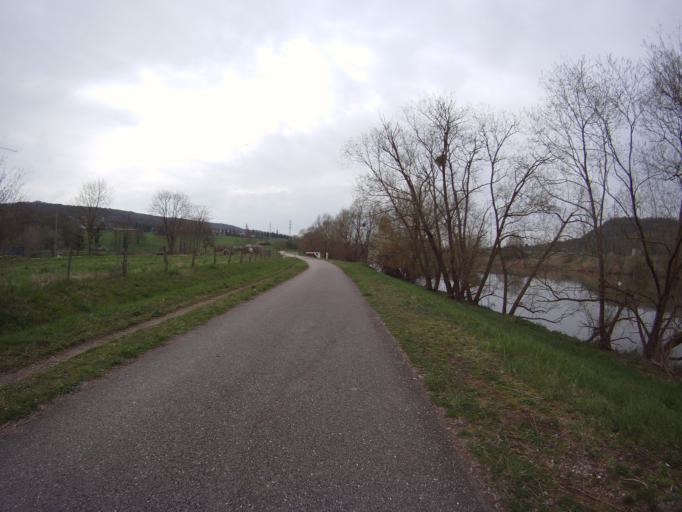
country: FR
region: Lorraine
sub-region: Departement de Meurthe-et-Moselle
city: Champigneulles
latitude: 48.7330
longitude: 6.1728
